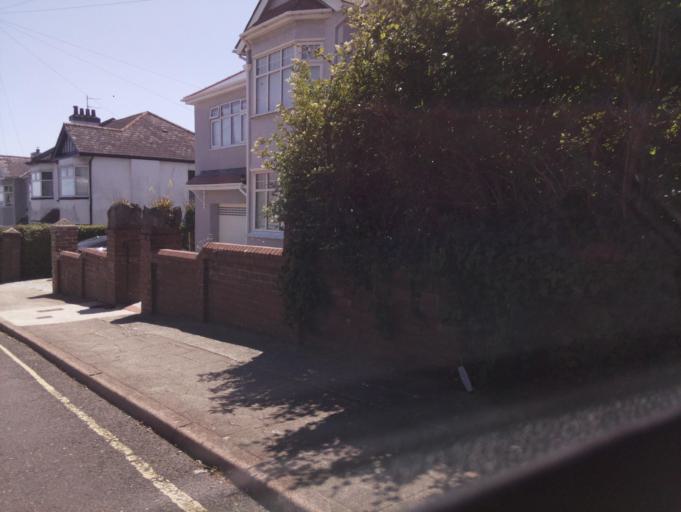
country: GB
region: England
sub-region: Borough of Torbay
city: Paignton
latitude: 50.4486
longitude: -3.5598
